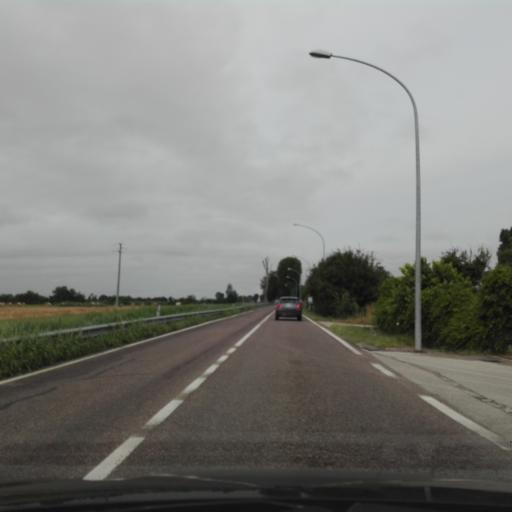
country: IT
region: Veneto
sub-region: Provincia di Rovigo
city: Grignano Polesine
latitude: 45.0790
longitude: 11.7547
